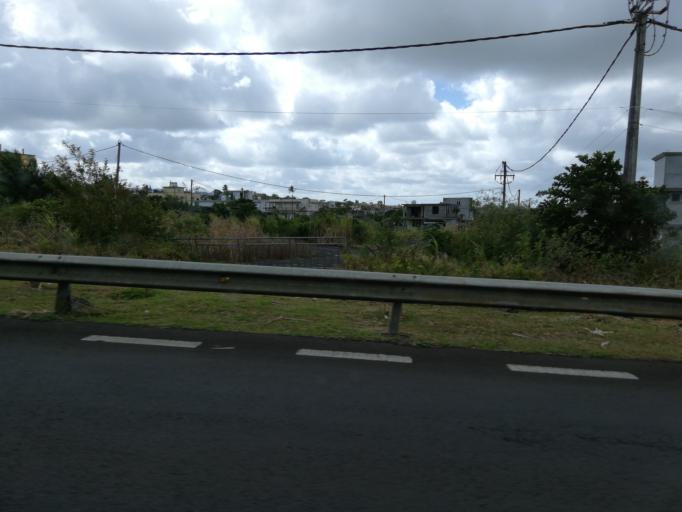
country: MU
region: Grand Port
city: Rose Belle
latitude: -20.3940
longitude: 57.5783
